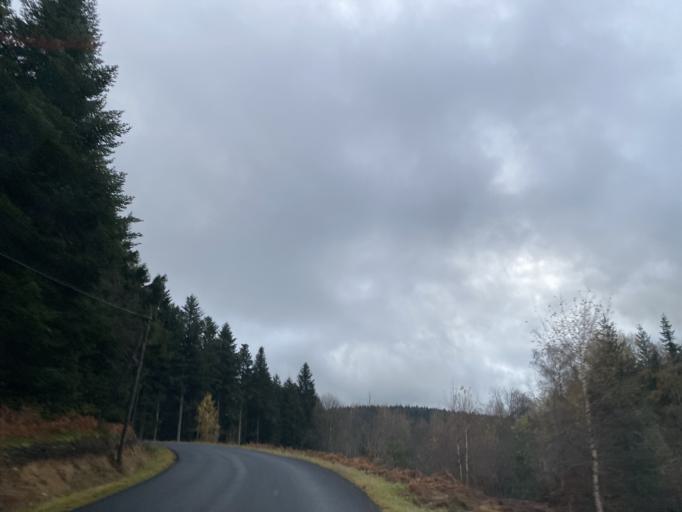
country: FR
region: Auvergne
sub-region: Departement du Puy-de-Dome
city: Cunlhat
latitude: 45.5690
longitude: 3.5657
